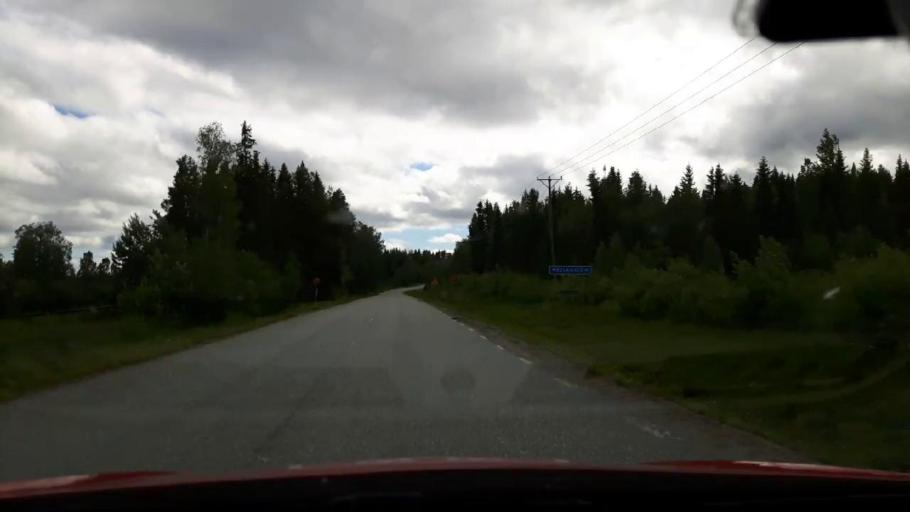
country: SE
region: Jaemtland
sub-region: Ragunda Kommun
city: Hammarstrand
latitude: 62.9656
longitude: 16.0618
